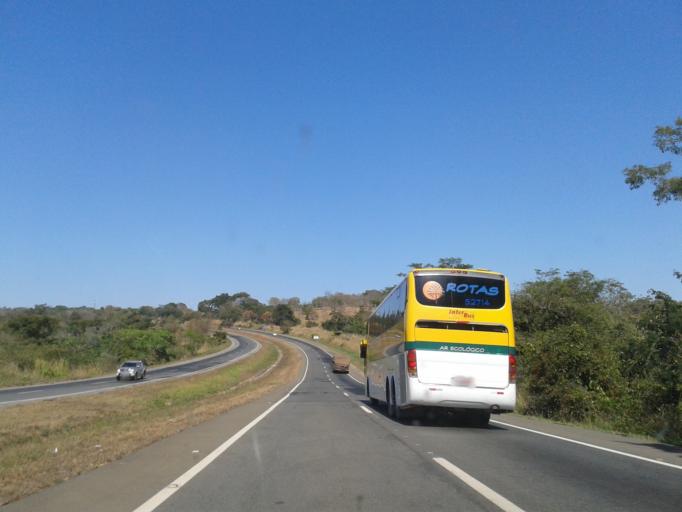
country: BR
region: Goias
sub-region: Piracanjuba
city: Piracanjuba
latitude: -17.2357
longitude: -49.2368
